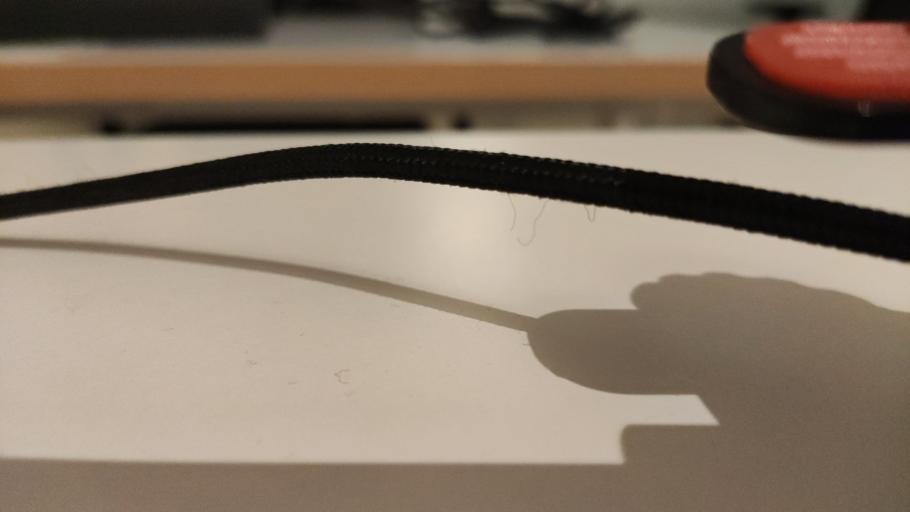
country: RU
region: Moskovskaya
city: Likino-Dulevo
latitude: 55.7037
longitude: 38.9574
